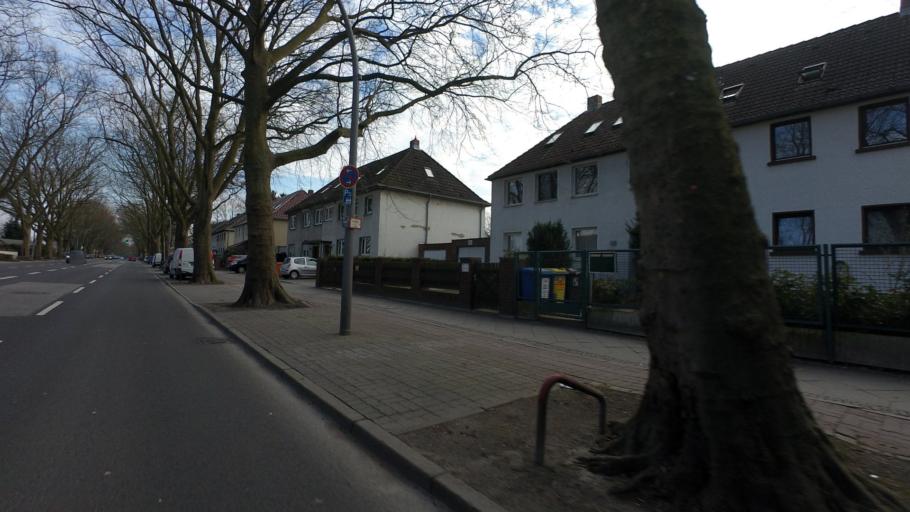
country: DE
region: Berlin
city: Reinickendorf
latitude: 52.5843
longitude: 13.3427
